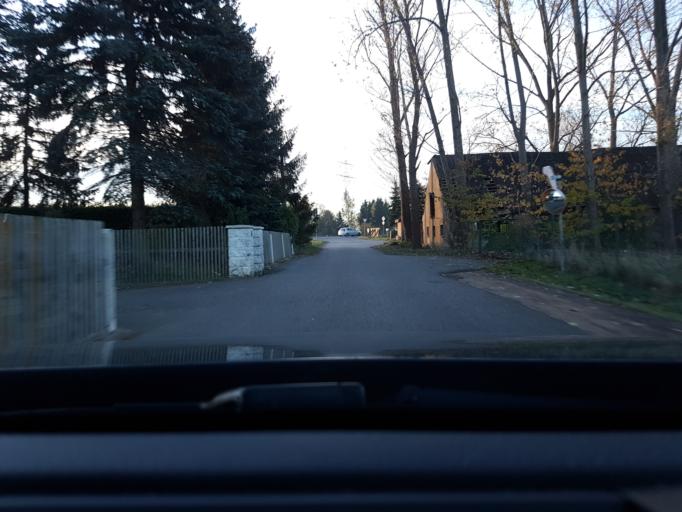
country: DE
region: Saxony
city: Altmittweida
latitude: 50.9530
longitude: 12.9711
